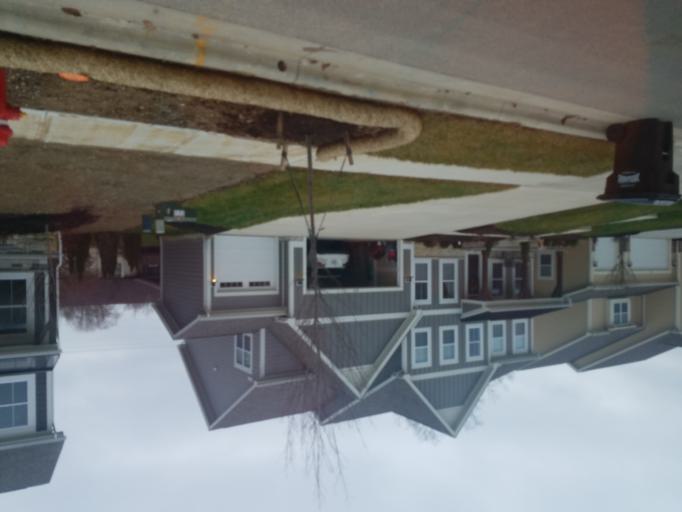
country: US
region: Ohio
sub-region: Franklin County
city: Westerville
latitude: 40.1310
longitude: -82.9564
